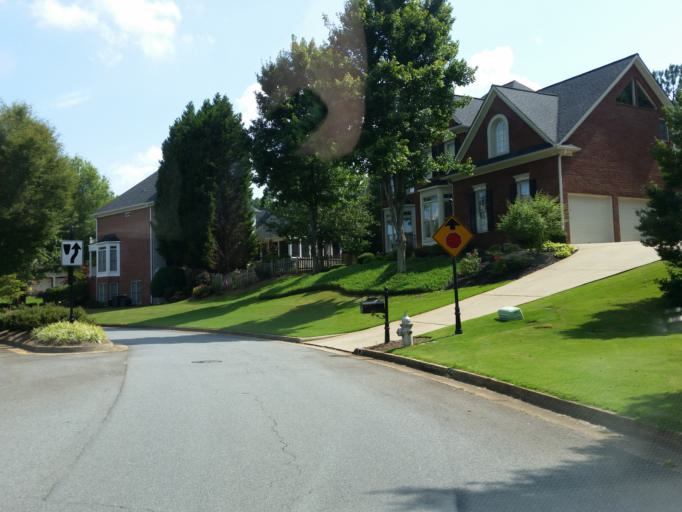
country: US
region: Georgia
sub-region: Cherokee County
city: Woodstock
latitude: 34.0352
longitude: -84.4715
